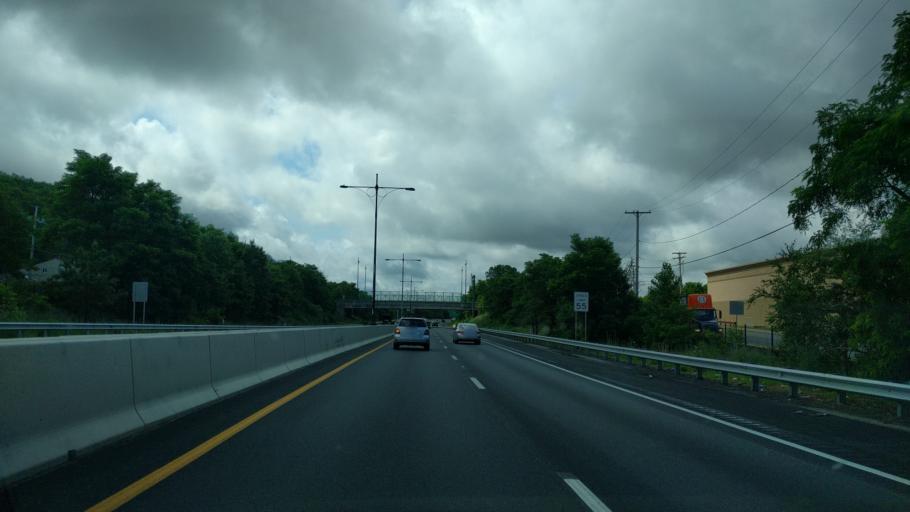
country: US
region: Massachusetts
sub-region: Worcester County
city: Sunderland
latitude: 42.2298
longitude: -71.7866
